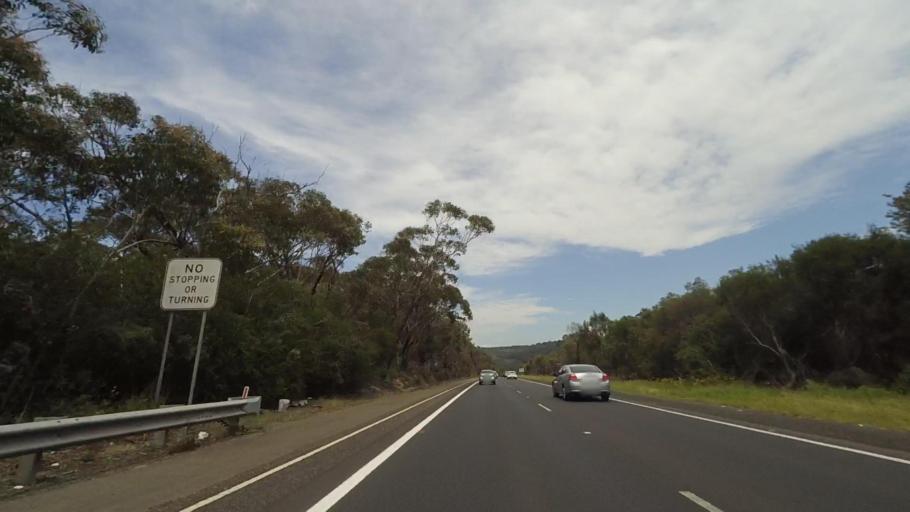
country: AU
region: New South Wales
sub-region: Wollongong
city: Helensburgh
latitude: -34.1543
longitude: 150.9878
